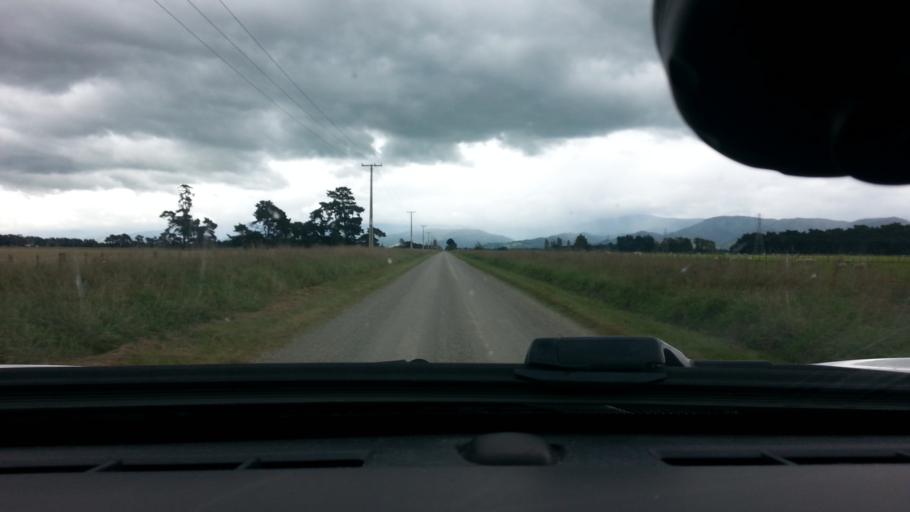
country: NZ
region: Wellington
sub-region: Masterton District
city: Masterton
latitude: -41.1191
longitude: 175.4301
